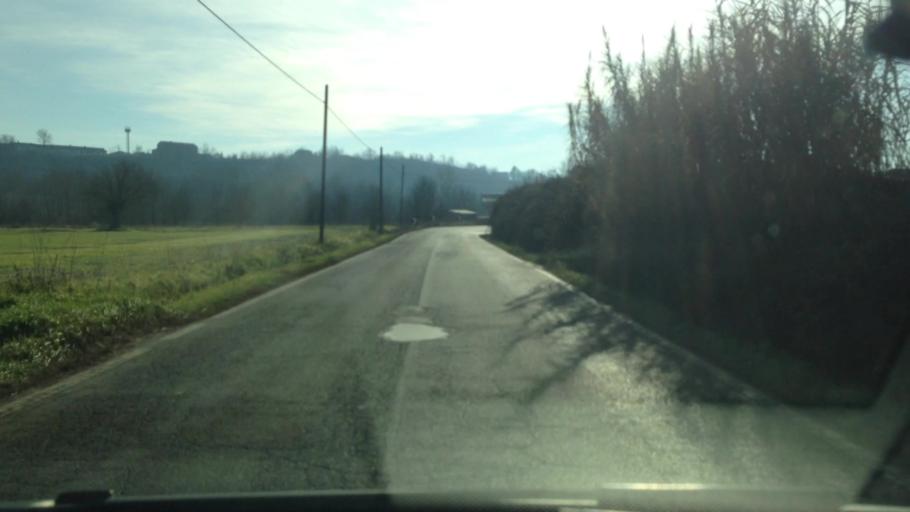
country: IT
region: Piedmont
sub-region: Provincia di Alessandria
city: Masio
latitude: 44.8661
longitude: 8.4165
